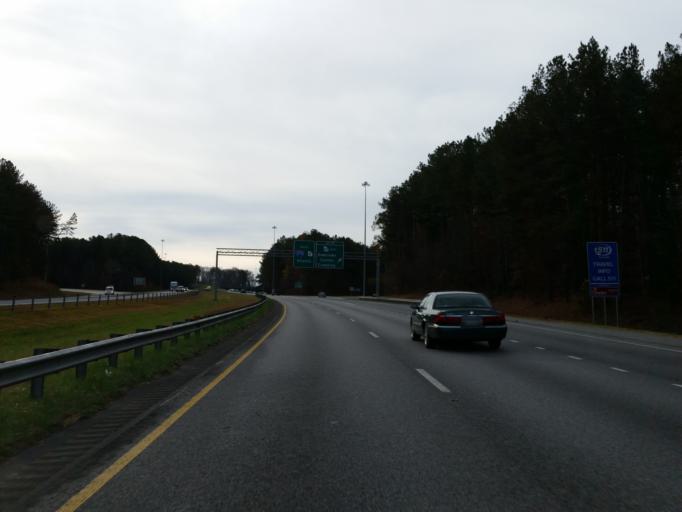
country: US
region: Georgia
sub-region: Cherokee County
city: Canton
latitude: 34.2449
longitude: -84.4675
